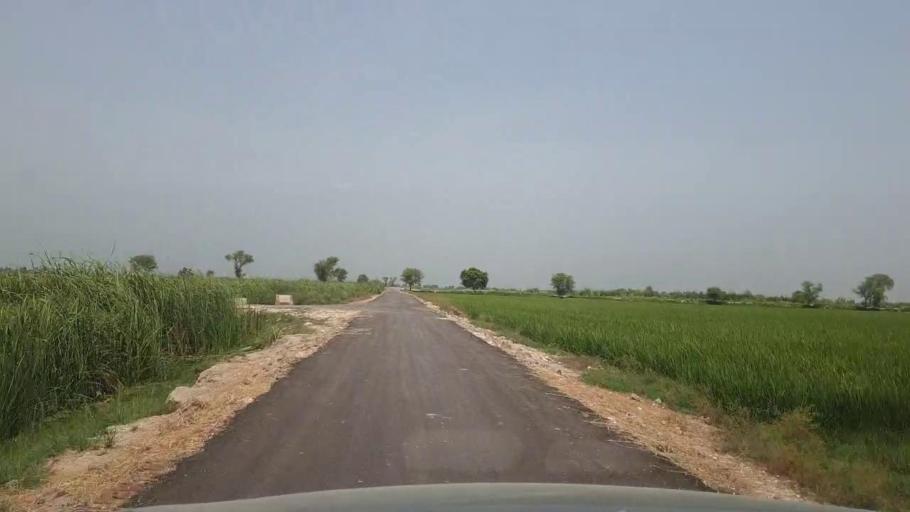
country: PK
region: Sindh
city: Garhi Yasin
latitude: 27.9299
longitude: 68.4326
